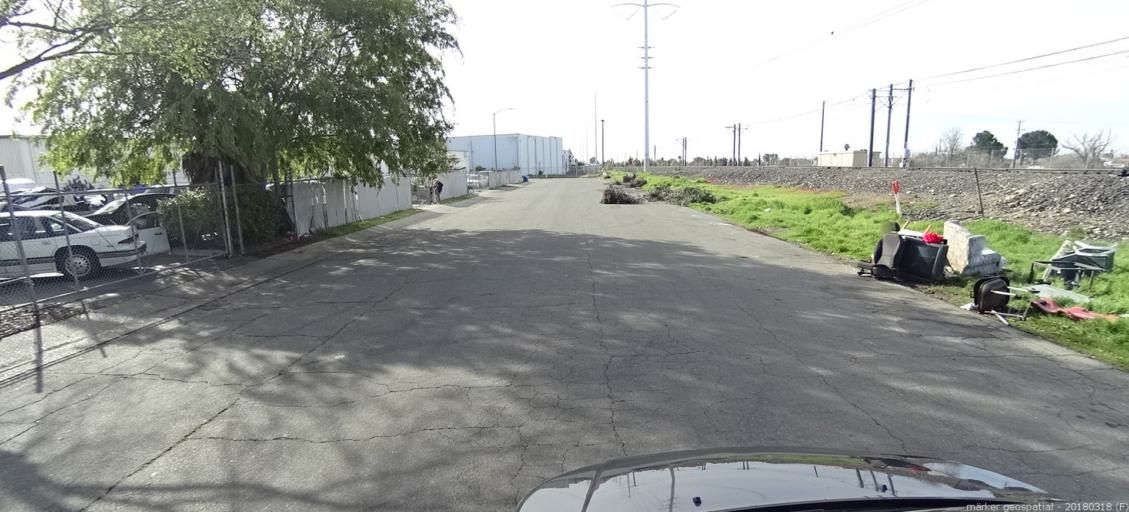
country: US
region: California
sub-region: Sacramento County
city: Parkway
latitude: 38.5041
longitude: -121.4731
